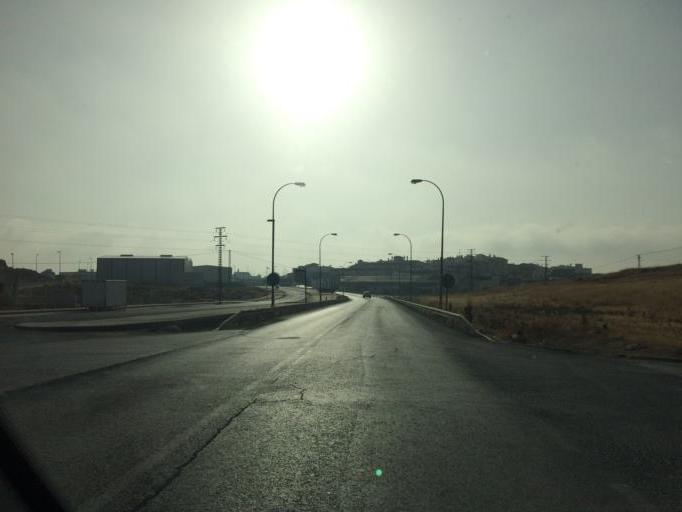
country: ES
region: Andalusia
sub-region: Provincia de Malaga
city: Campillos
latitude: 37.0518
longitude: -4.8693
